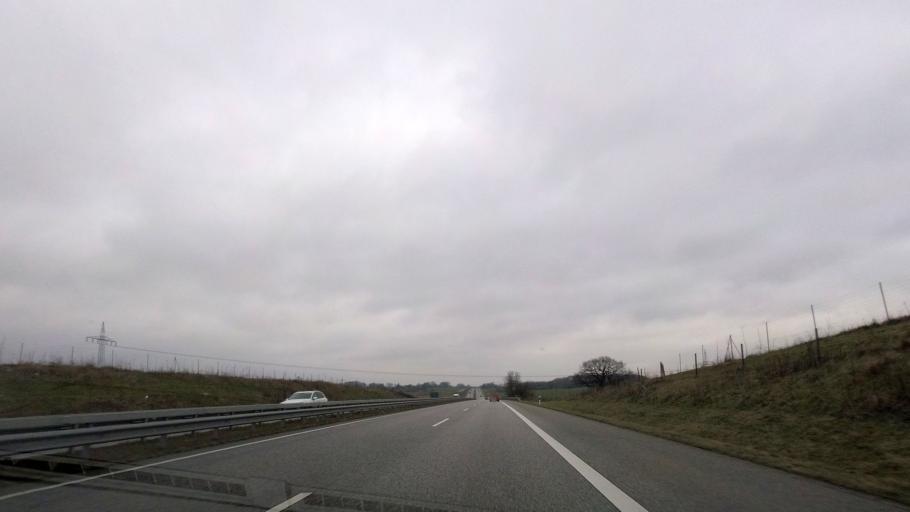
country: DE
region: Schleswig-Holstein
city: Stolpe
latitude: 54.1413
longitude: 10.2121
